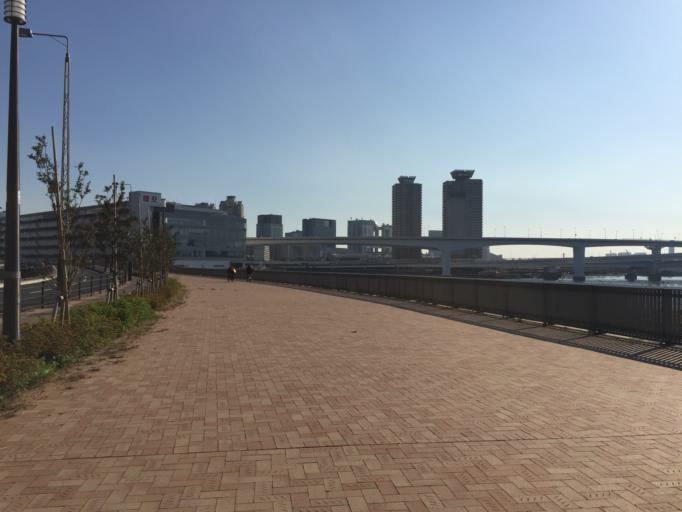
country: JP
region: Tokyo
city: Tokyo
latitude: 35.6407
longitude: 139.7795
